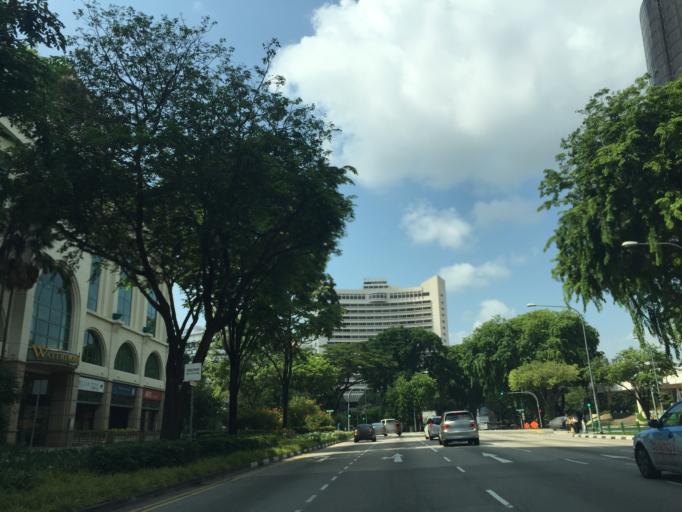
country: SG
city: Singapore
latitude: 1.2902
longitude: 103.8347
